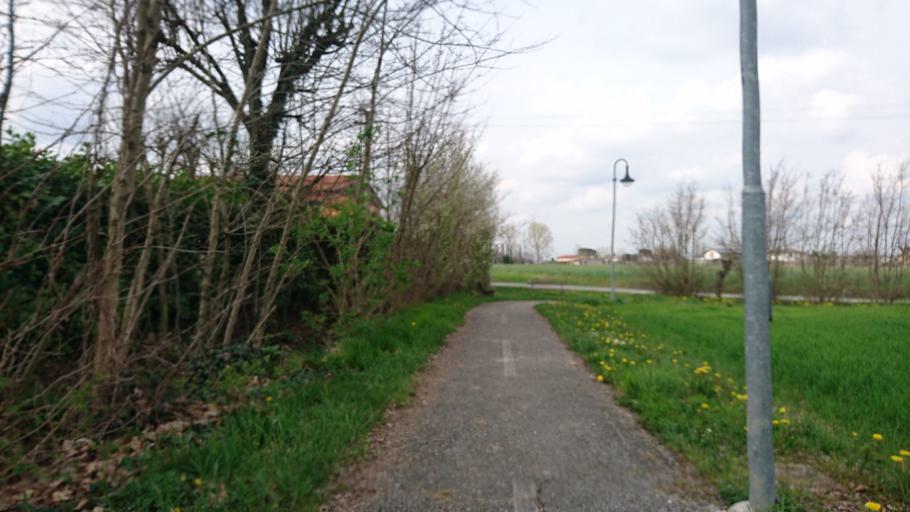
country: IT
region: Veneto
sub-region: Provincia di Padova
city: Tremignon
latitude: 45.4984
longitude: 11.8218
